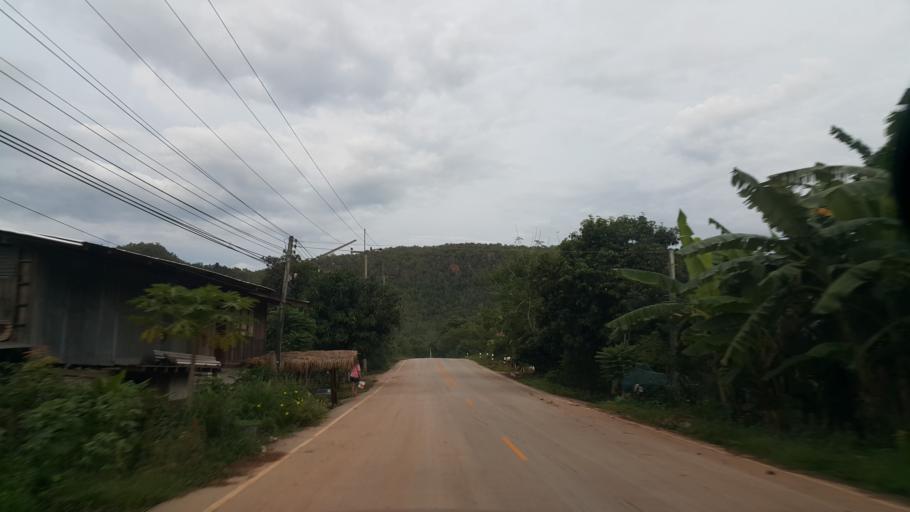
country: TH
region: Loei
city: Na Haeo
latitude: 17.4939
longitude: 101.1794
